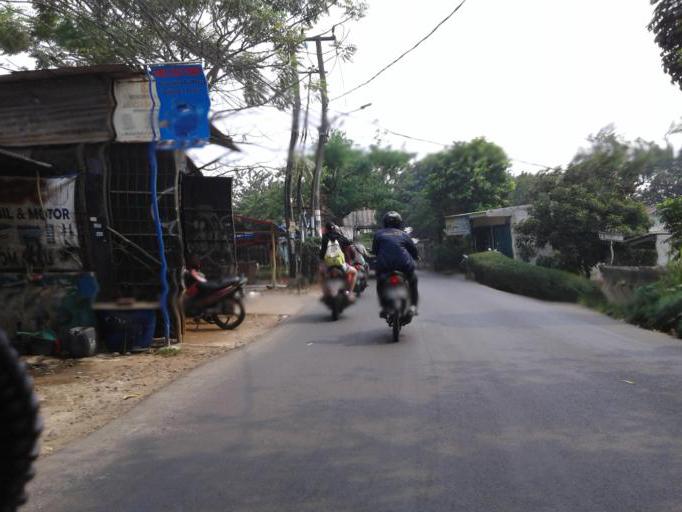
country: ID
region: Banten
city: South Tangerang
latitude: -6.2920
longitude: 106.7429
